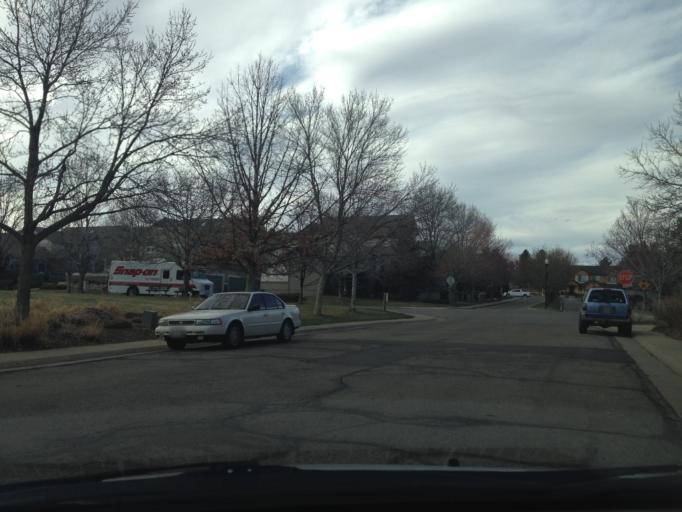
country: US
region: Colorado
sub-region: Boulder County
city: Louisville
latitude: 39.9989
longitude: -105.1164
